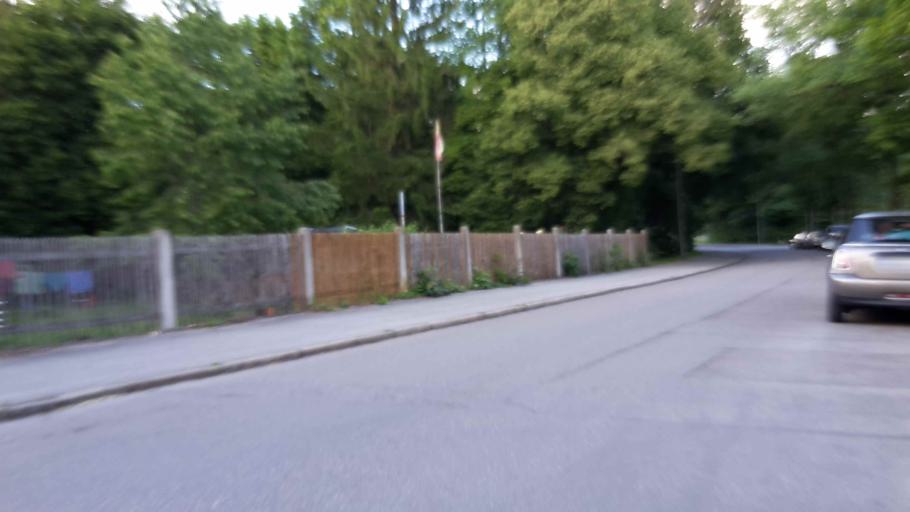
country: DE
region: Bavaria
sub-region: Upper Bavaria
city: Unterfoehring
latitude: 48.1946
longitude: 11.6190
